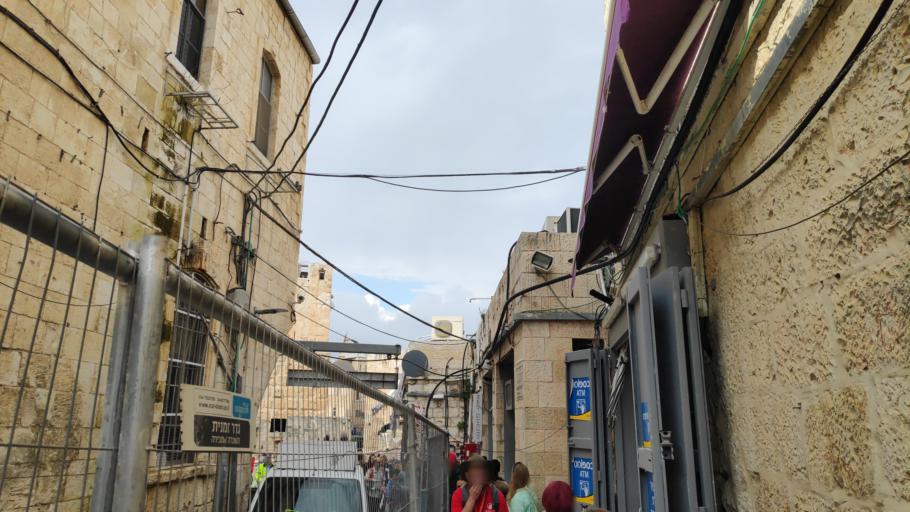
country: PS
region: West Bank
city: Old City
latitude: 31.7756
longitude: 35.2289
